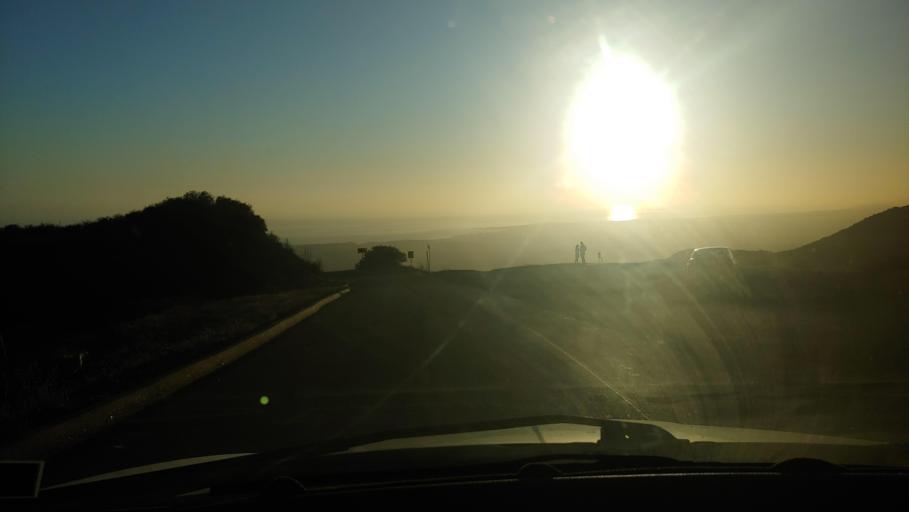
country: US
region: California
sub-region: Santa Barbara County
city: Mission Canyon
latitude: 34.4710
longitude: -119.6790
